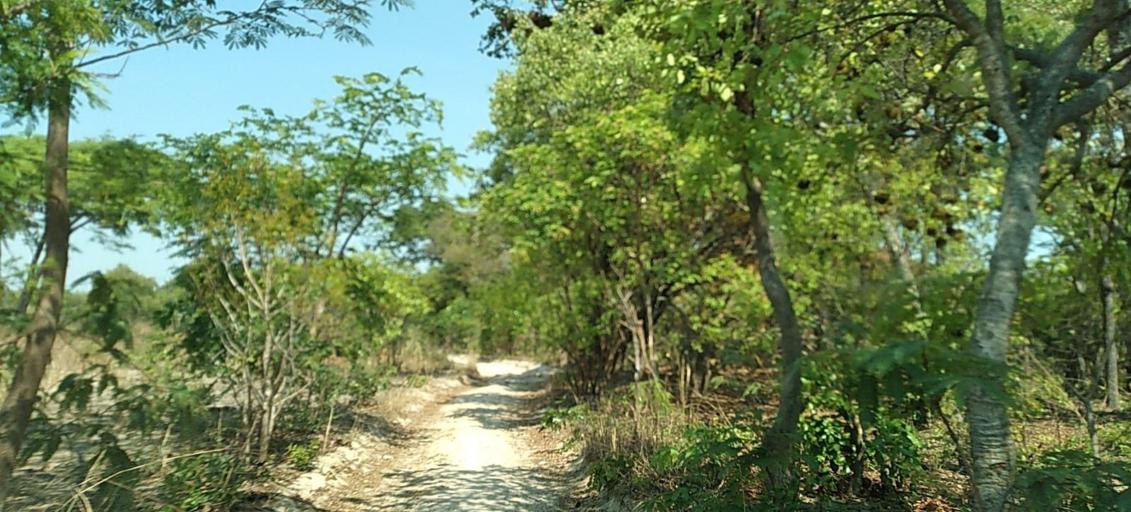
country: ZM
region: Copperbelt
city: Mpongwe
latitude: -13.7768
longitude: 28.1088
